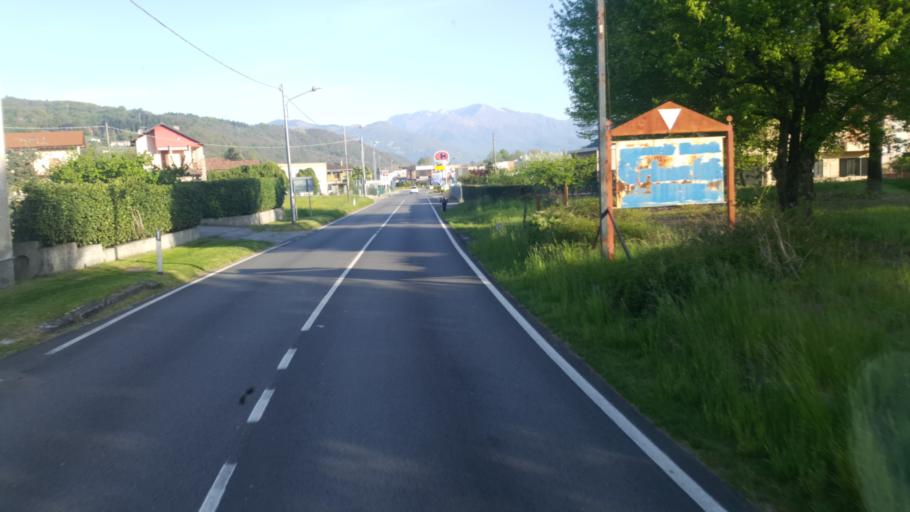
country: IT
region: Lombardy
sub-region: Provincia di Varese
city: Mesenzana
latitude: 45.9552
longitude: 8.7630
